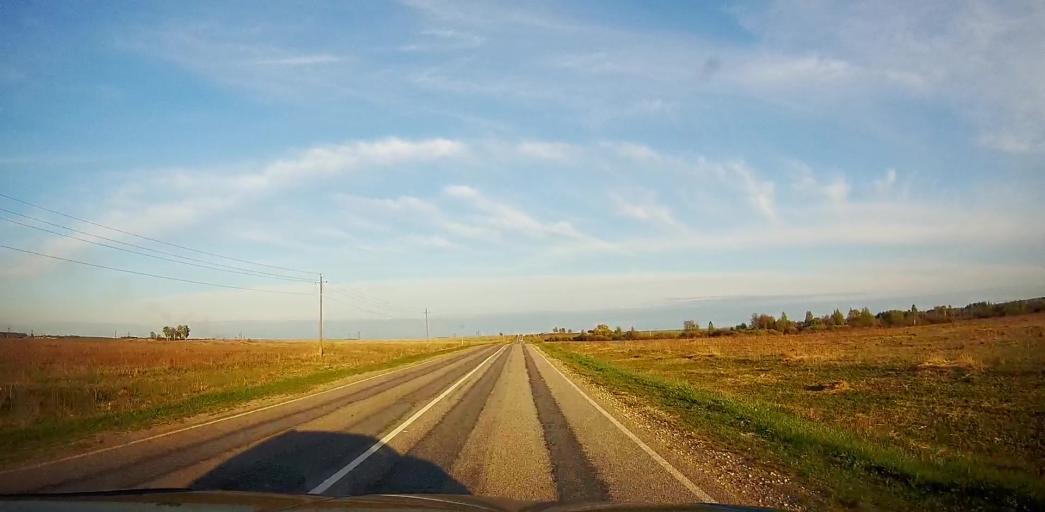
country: RU
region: Moskovskaya
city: Meshcherino
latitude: 55.2728
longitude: 38.2336
